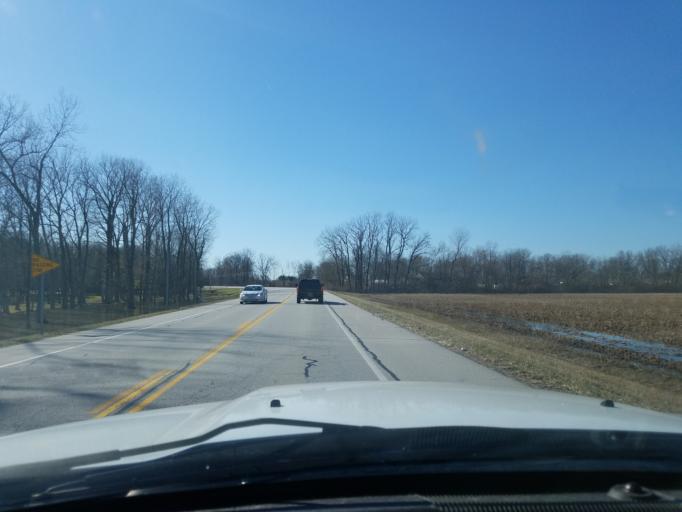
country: US
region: Indiana
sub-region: Johnson County
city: Franklin
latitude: 39.4953
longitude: -85.9615
